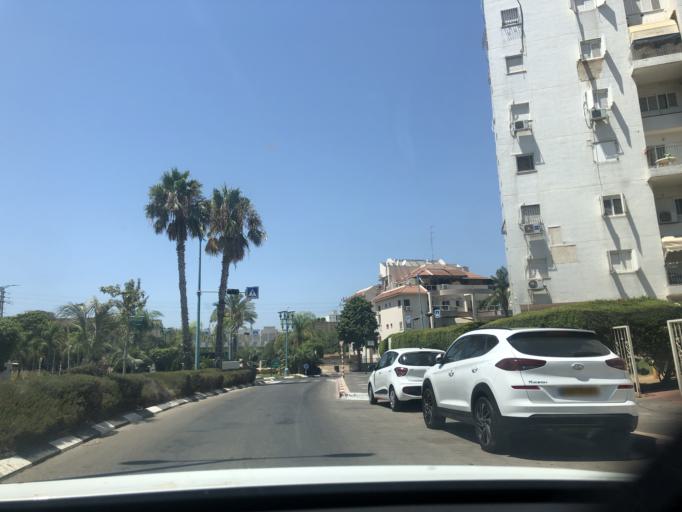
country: IL
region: Central District
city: Lod
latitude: 31.9458
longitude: 34.9054
